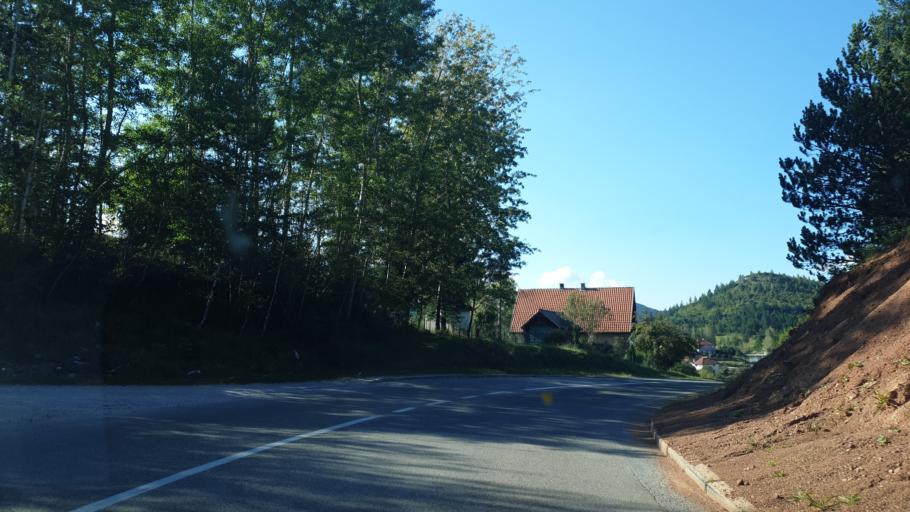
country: RS
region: Central Serbia
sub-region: Zlatiborski Okrug
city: Nova Varos
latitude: 43.5405
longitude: 19.7890
